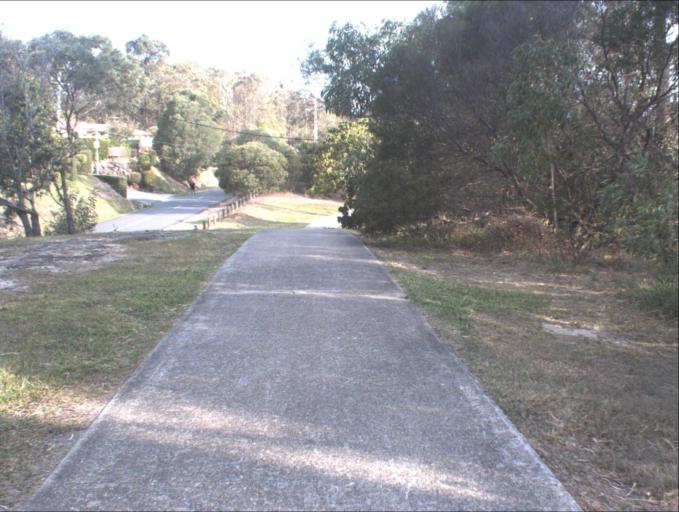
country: AU
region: Queensland
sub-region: Logan
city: Slacks Creek
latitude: -27.6282
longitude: 153.1461
